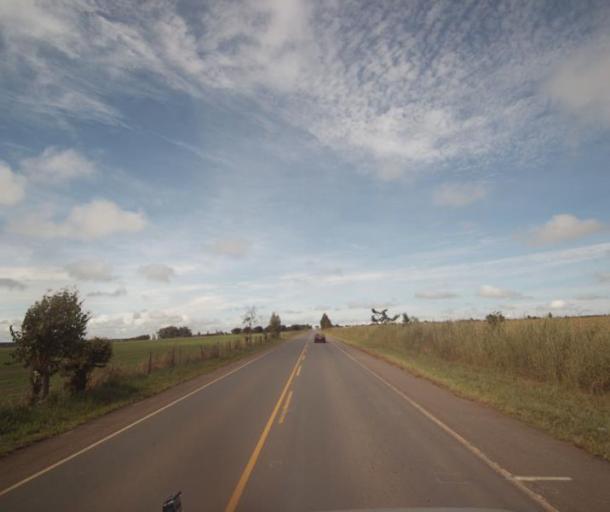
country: BR
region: Goias
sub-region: Abadiania
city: Abadiania
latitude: -16.0413
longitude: -48.8522
